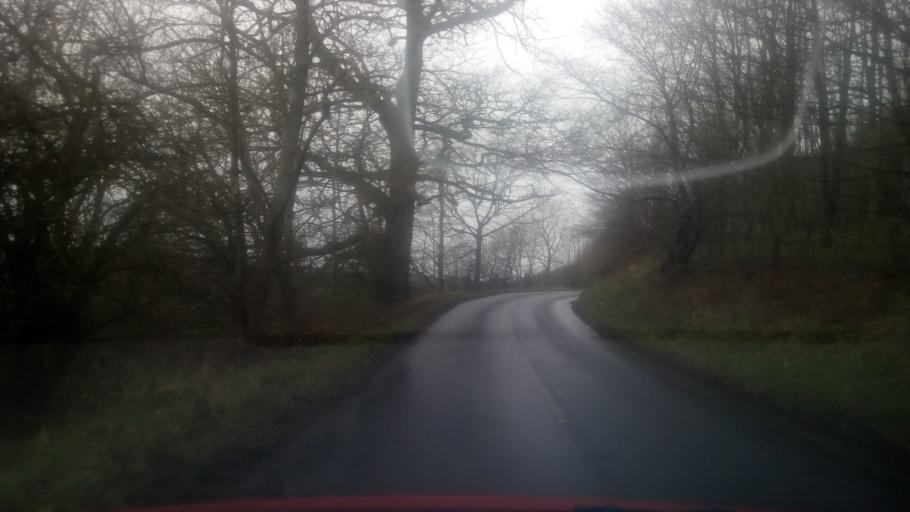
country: GB
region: Scotland
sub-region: The Scottish Borders
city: Earlston
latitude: 55.6212
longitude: -2.6659
